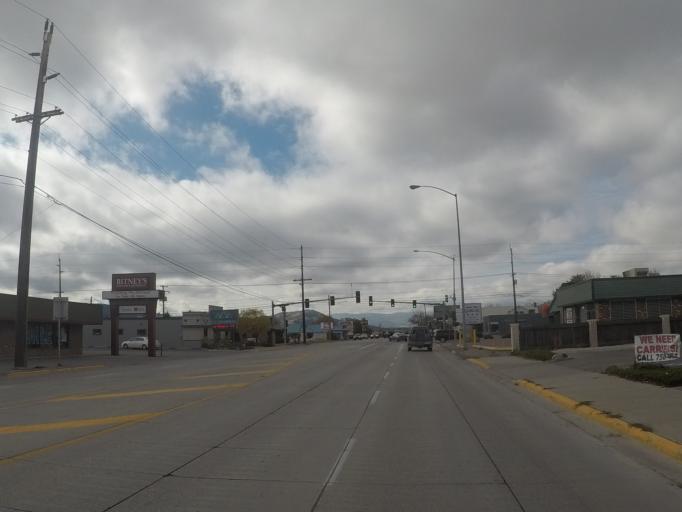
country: US
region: Montana
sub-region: Flathead County
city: Kalispell
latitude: 48.2044
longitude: -114.3018
